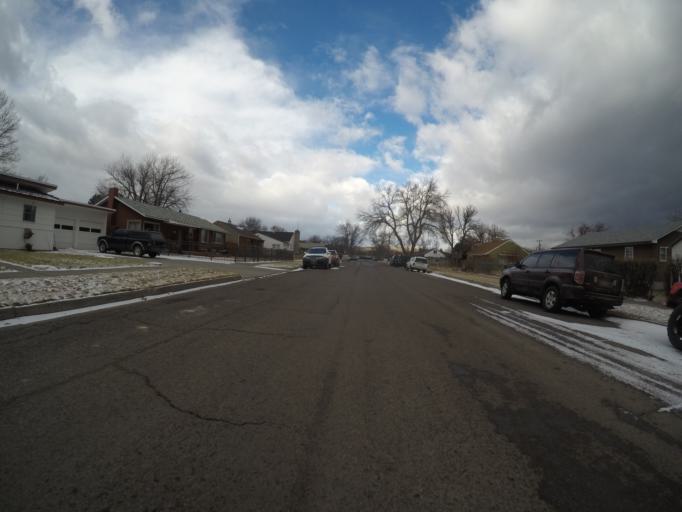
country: US
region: Montana
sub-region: Park County
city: Livingston
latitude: 45.6504
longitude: -110.5698
